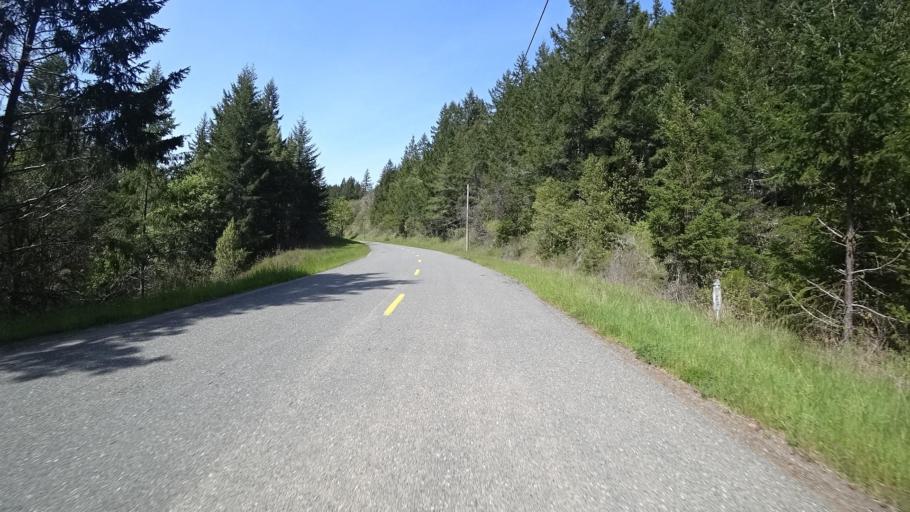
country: US
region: California
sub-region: Humboldt County
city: Rio Dell
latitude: 40.4470
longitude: -123.7953
